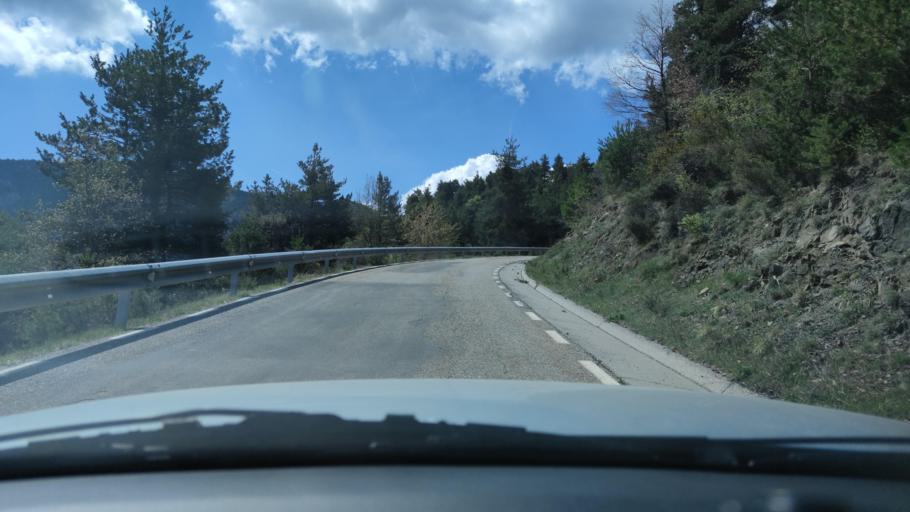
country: ES
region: Catalonia
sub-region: Provincia de Lleida
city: Coll de Nargo
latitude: 42.2921
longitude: 1.2465
